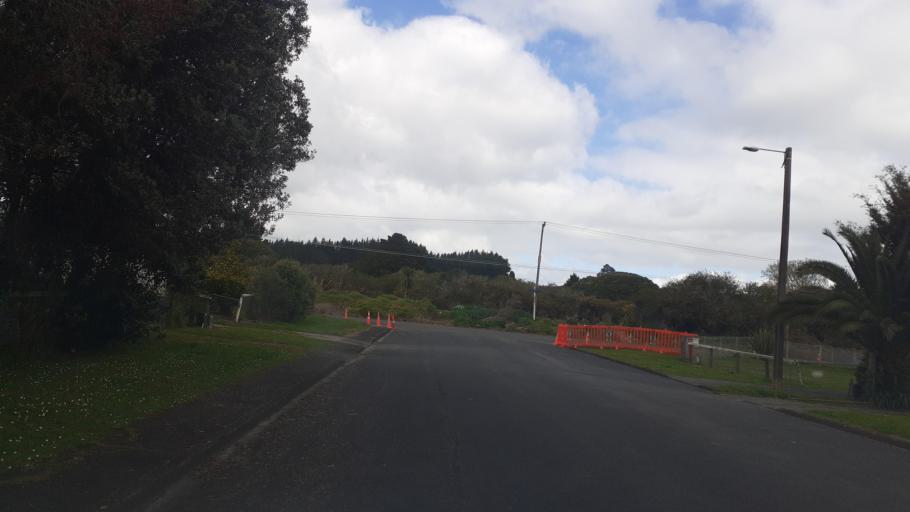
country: NZ
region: Northland
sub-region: Far North District
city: Moerewa
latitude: -35.3903
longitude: 174.0172
